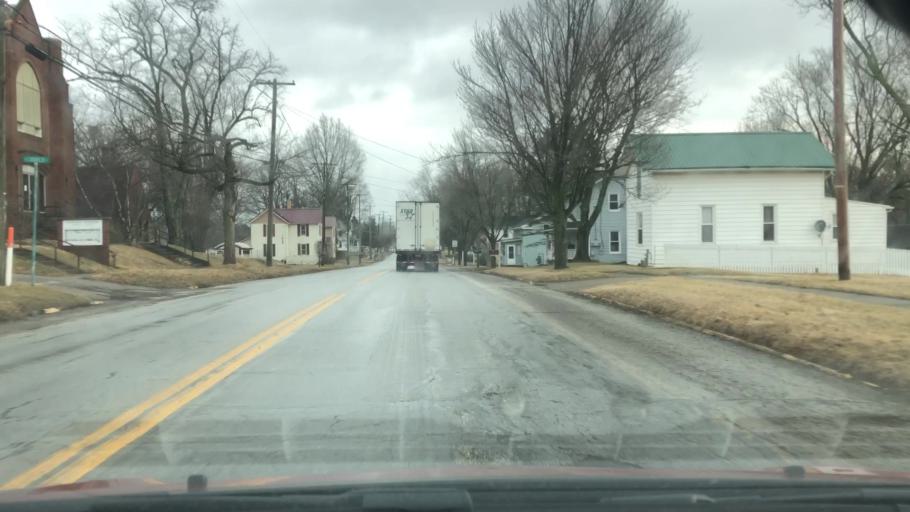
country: US
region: Ohio
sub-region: Wayne County
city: Smithville
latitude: 40.8647
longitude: -81.8574
